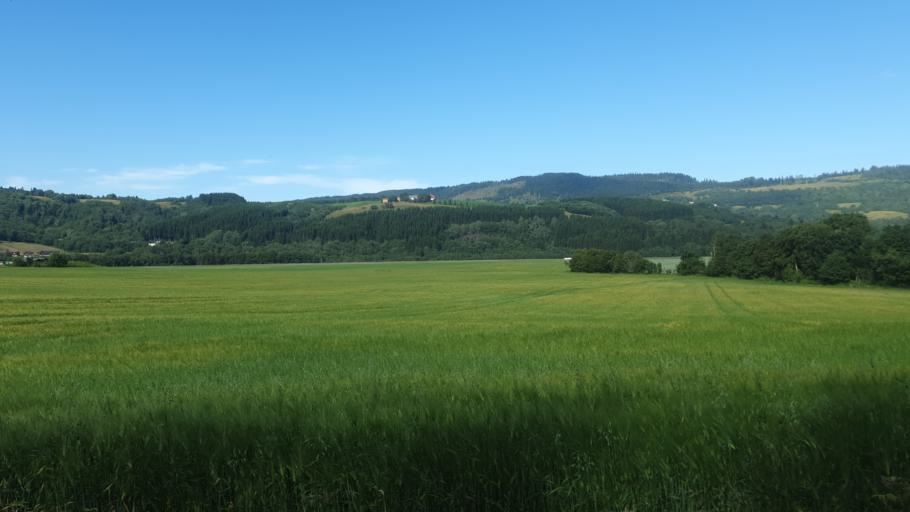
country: NO
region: Sor-Trondelag
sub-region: Orkdal
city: Orkanger
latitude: 63.2693
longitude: 9.8172
